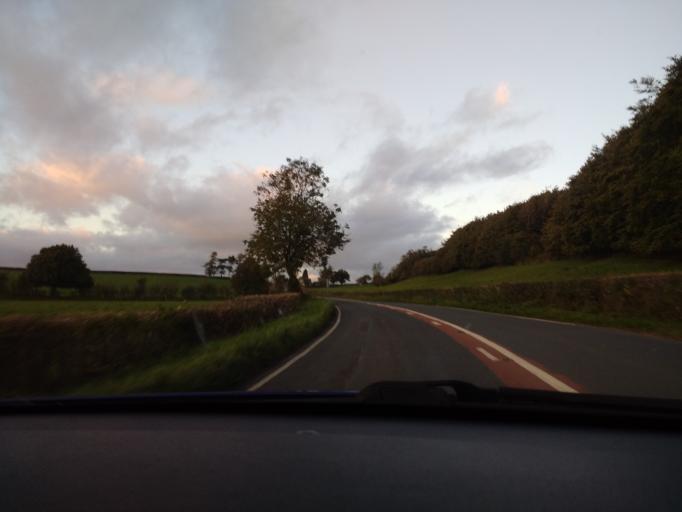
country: GB
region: England
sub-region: Lancashire
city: Caton
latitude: 54.1246
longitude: -2.6308
